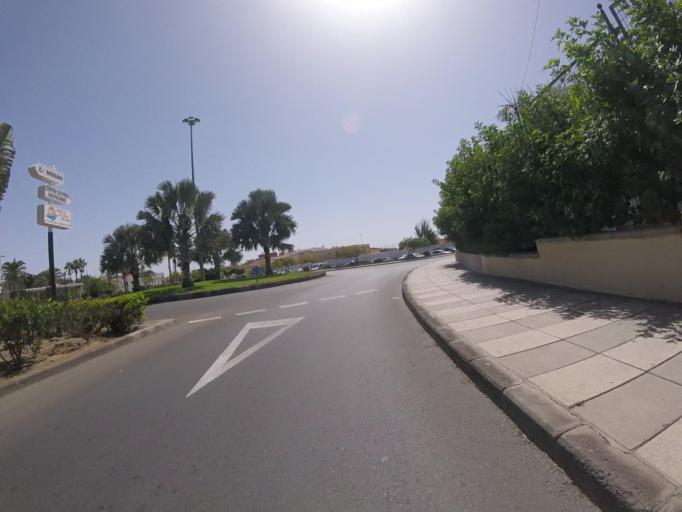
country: ES
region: Canary Islands
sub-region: Provincia de Las Palmas
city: Maspalomas
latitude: 27.7672
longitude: -15.5823
